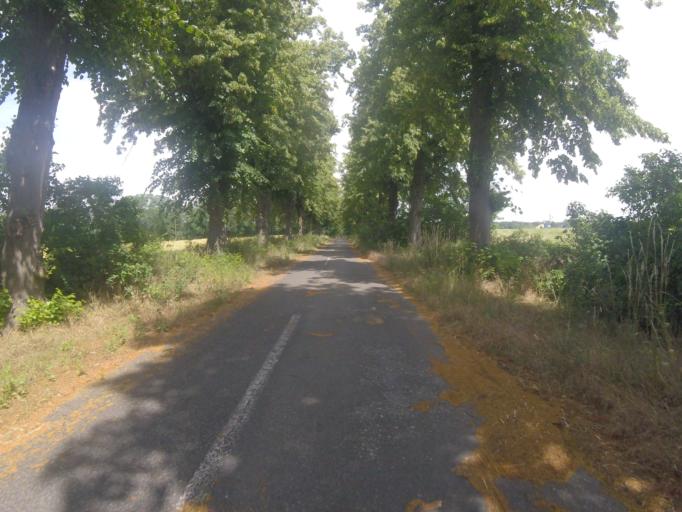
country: DE
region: Brandenburg
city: Konigs Wusterhausen
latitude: 52.3050
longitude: 13.5907
